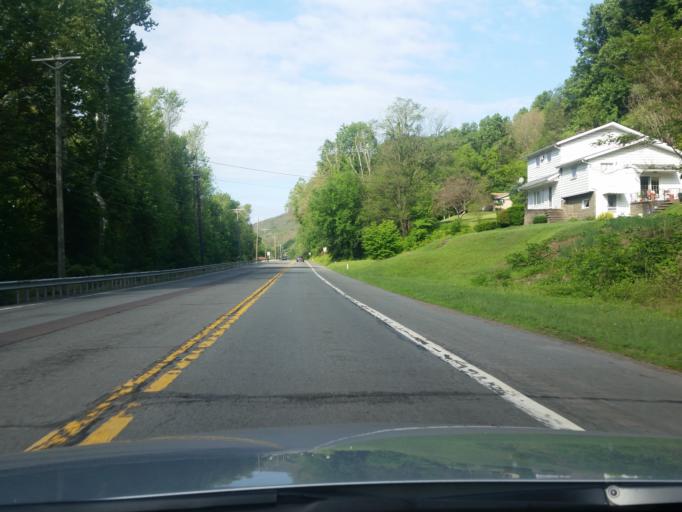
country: US
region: Pennsylvania
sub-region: Luzerne County
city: Glen Lyon
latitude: 41.1753
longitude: -76.1190
